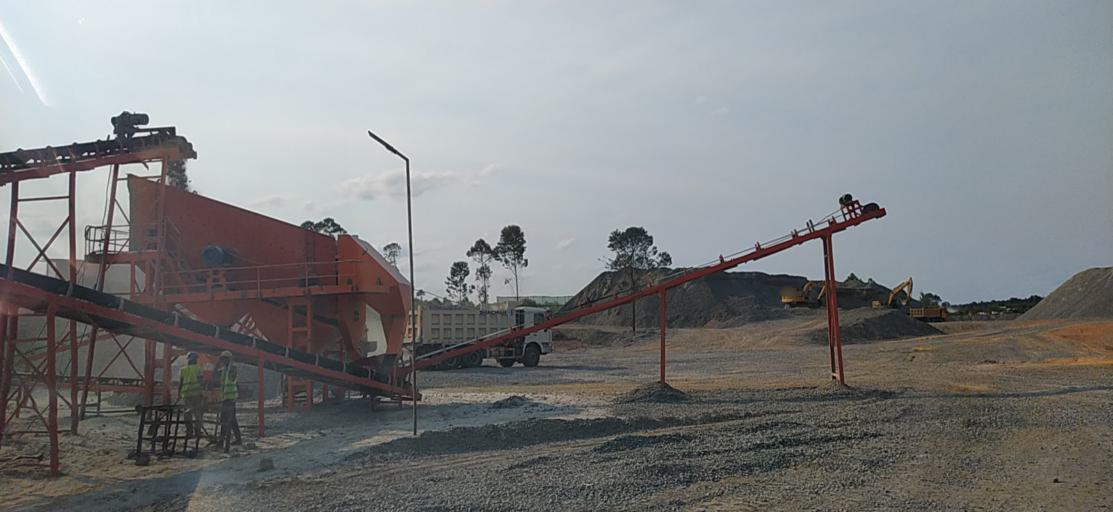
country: MG
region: Alaotra Mangoro
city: Moramanga
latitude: -18.6696
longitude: 48.2751
